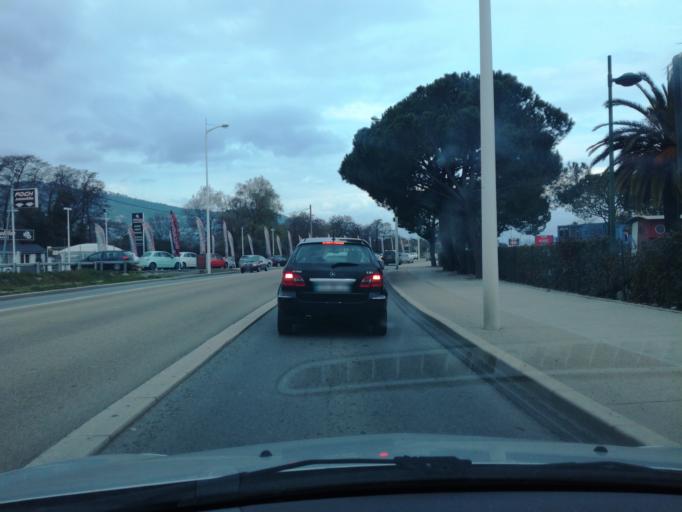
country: FR
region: Provence-Alpes-Cote d'Azur
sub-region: Departement des Alpes-Maritimes
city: Mandelieu-la-Napoule
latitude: 43.5513
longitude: 6.9561
